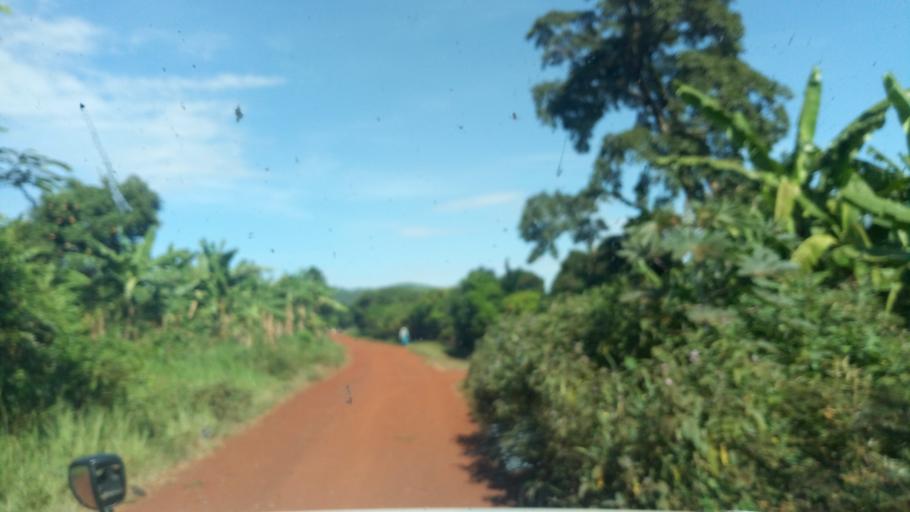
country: UG
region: Western Region
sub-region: Masindi District
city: Masindi
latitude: 1.6415
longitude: 31.7594
